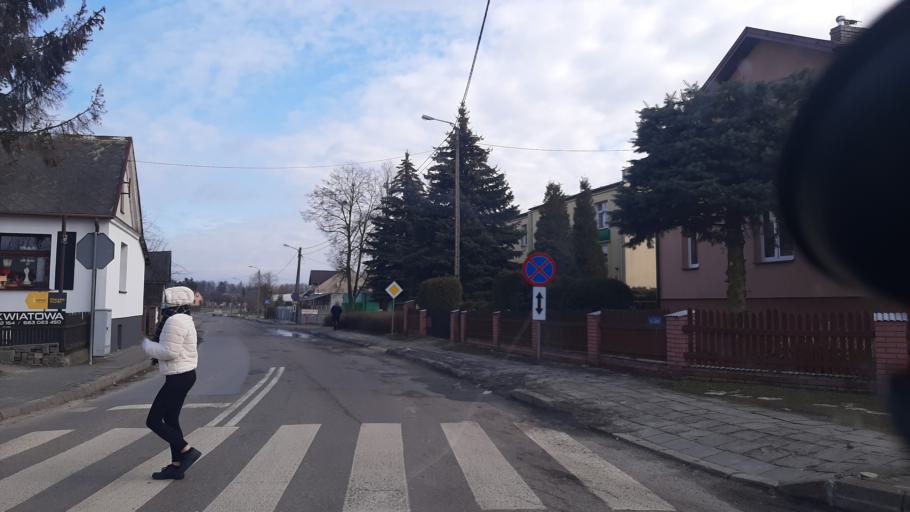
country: PL
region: Lublin Voivodeship
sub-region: Powiat lubartowski
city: Ostrow Lubelski
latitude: 51.4939
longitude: 22.8529
